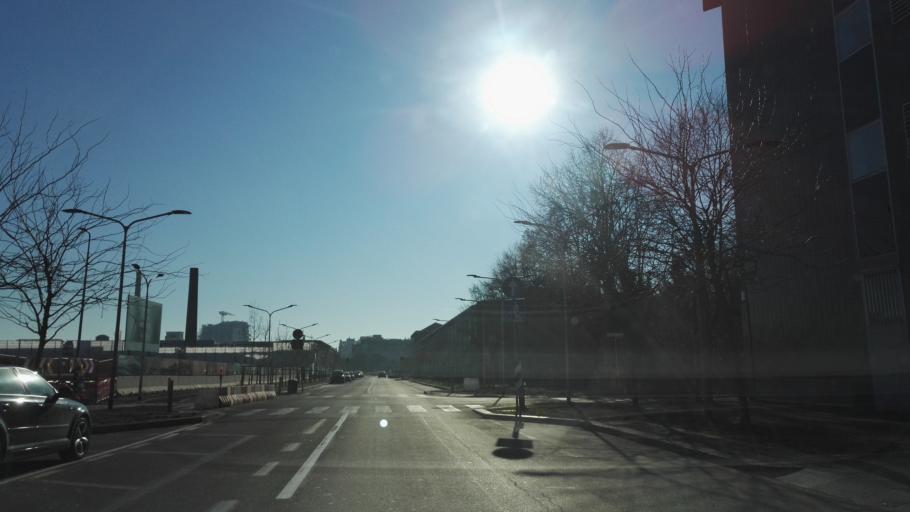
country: IT
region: Lombardy
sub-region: Citta metropolitana di Milano
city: Milano
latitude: 45.4417
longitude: 9.2032
